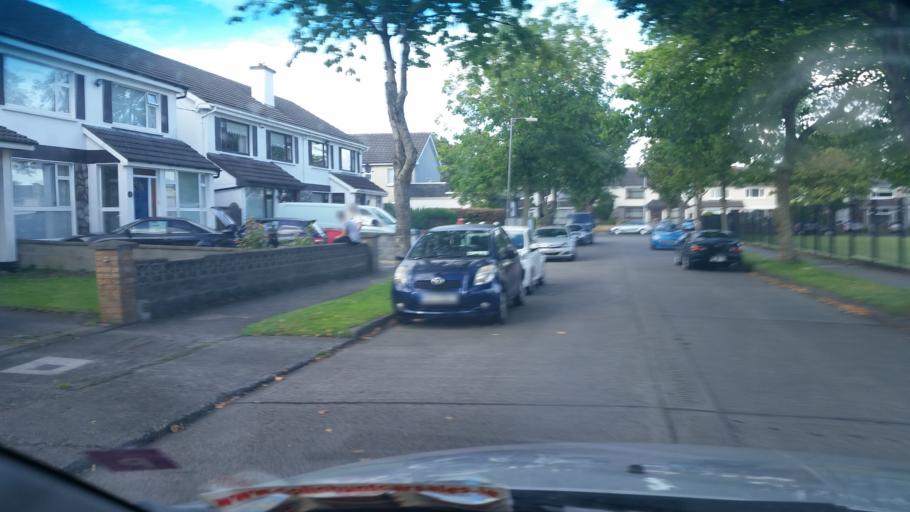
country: IE
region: Leinster
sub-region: Fingal County
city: Blanchardstown
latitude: 53.3844
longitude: -6.3836
